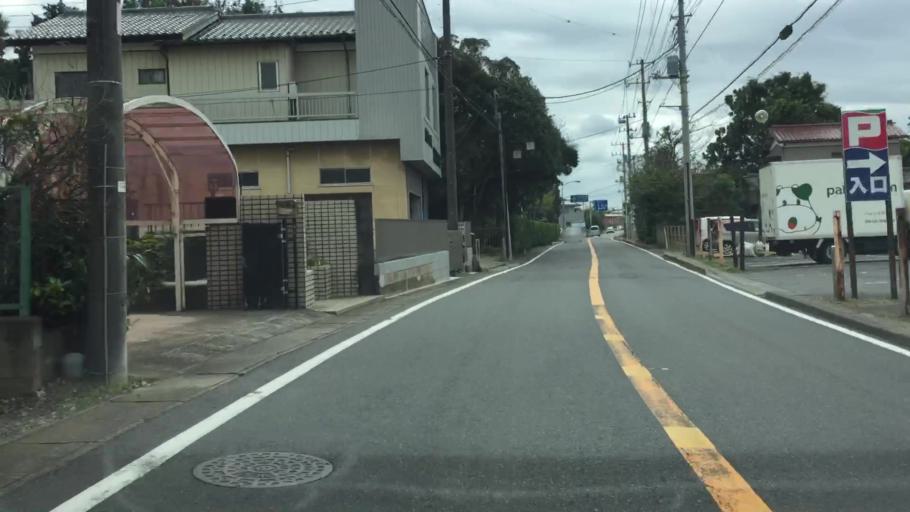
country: JP
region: Ibaraki
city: Ryugasaki
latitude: 35.8516
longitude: 140.1388
